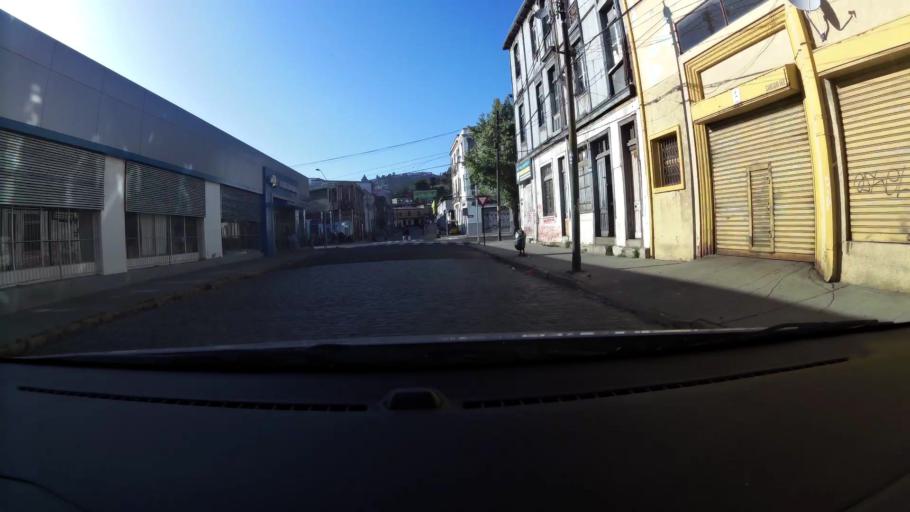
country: CL
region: Valparaiso
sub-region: Provincia de Valparaiso
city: Valparaiso
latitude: -33.0513
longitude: -71.6038
